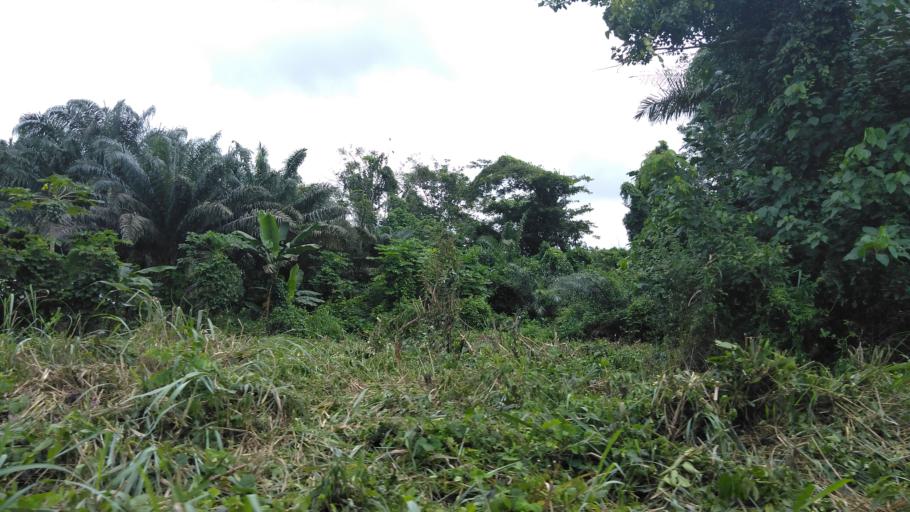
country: NG
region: Ogun
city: Abigi
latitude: 6.5951
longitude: 4.4967
